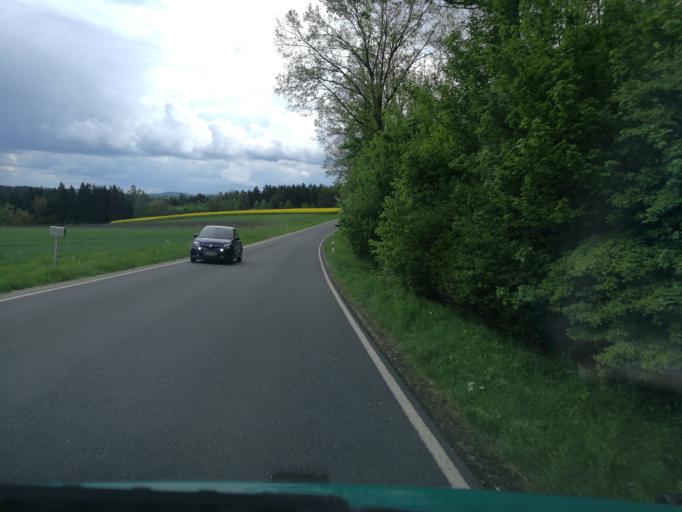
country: DE
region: Bavaria
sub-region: Upper Franconia
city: Michelau
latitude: 50.1889
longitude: 11.1167
